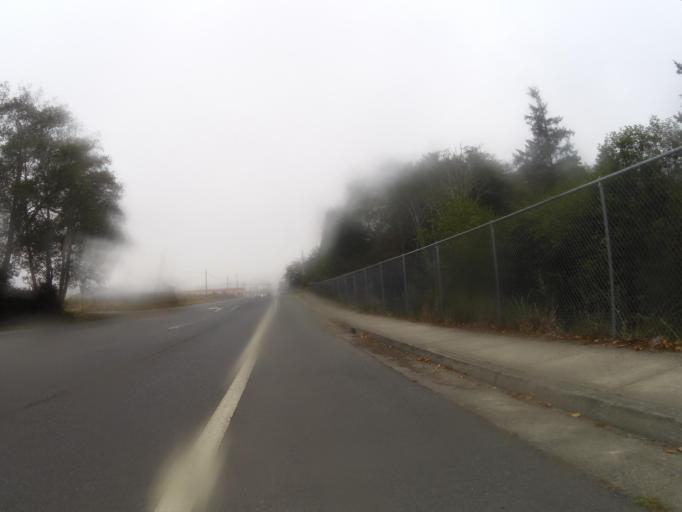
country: US
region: California
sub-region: Del Norte County
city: Crescent City
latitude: 41.7728
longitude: -124.1968
